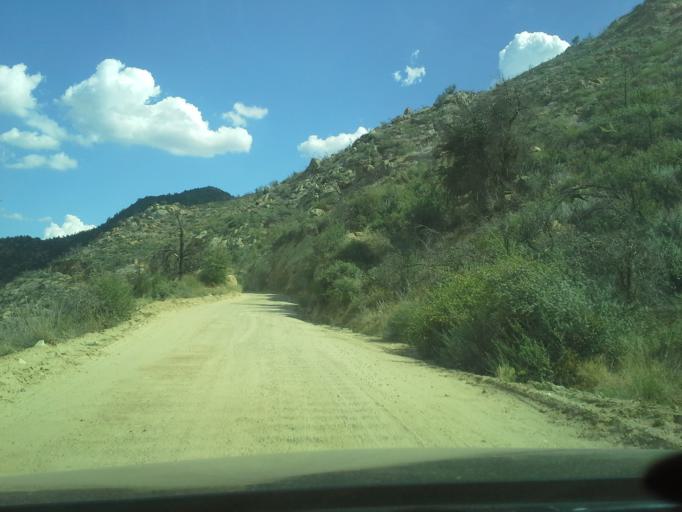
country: US
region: Arizona
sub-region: Yavapai County
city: Mayer
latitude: 34.2516
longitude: -112.3020
